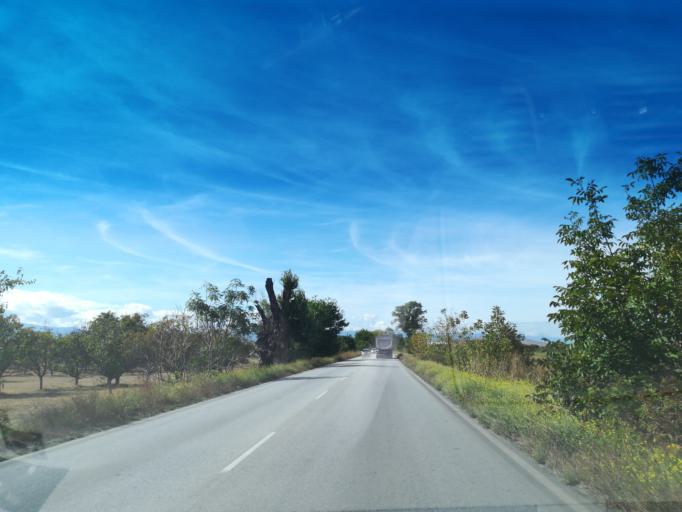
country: BG
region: Plovdiv
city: Stamboliyski
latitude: 42.1180
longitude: 24.5405
